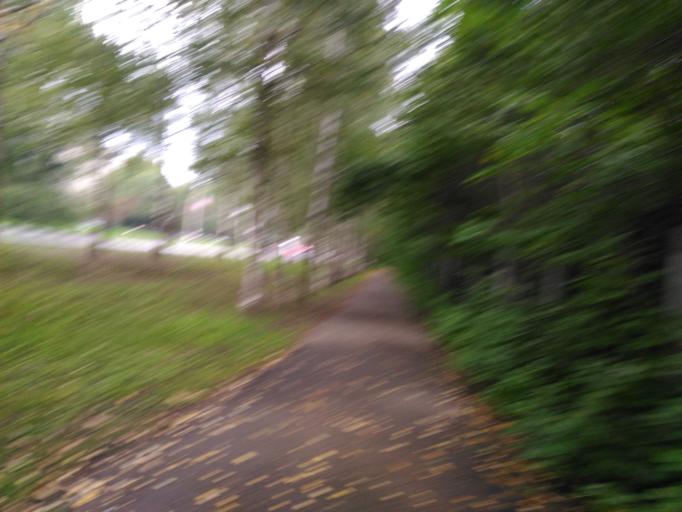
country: RU
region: Ulyanovsk
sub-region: Ulyanovskiy Rayon
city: Ulyanovsk
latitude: 54.2701
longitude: 48.3349
